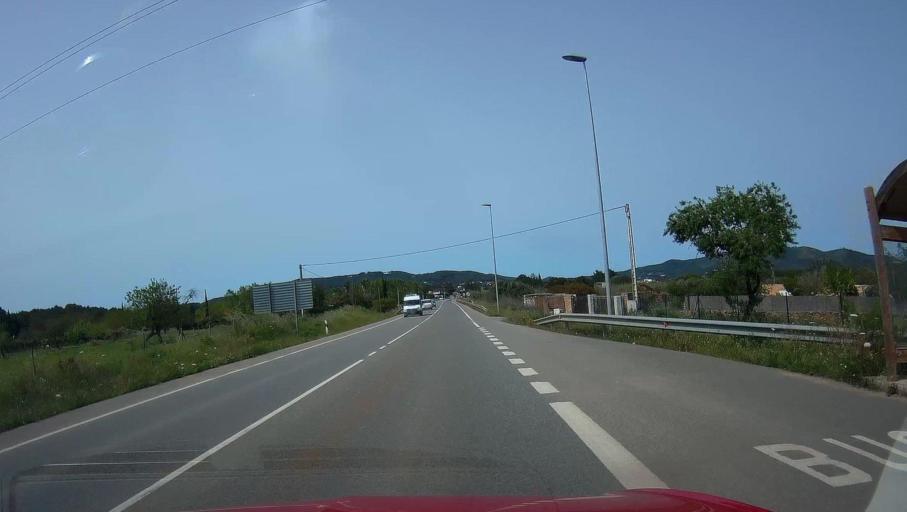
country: ES
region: Balearic Islands
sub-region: Illes Balears
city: Santa Eularia des Riu
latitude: 39.0068
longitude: 1.4882
